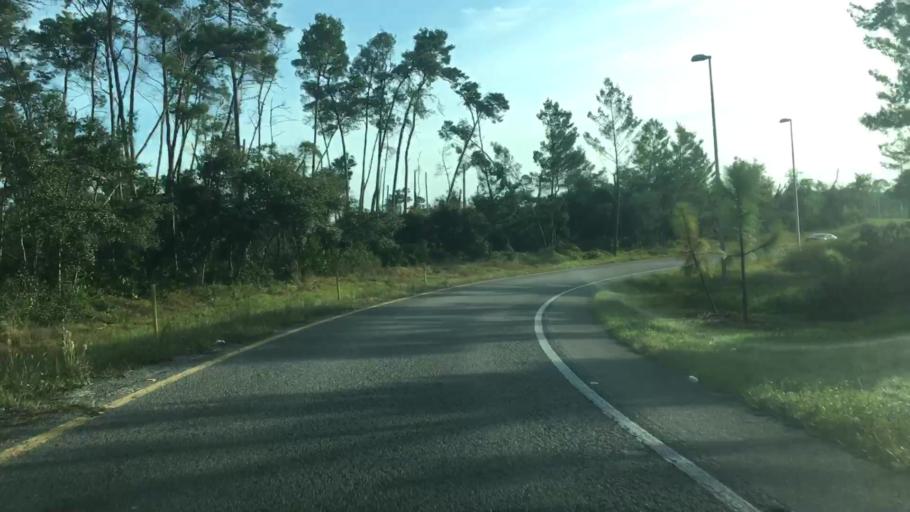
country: US
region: Florida
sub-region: Volusia County
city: Deltona
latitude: 28.9130
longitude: -81.2731
